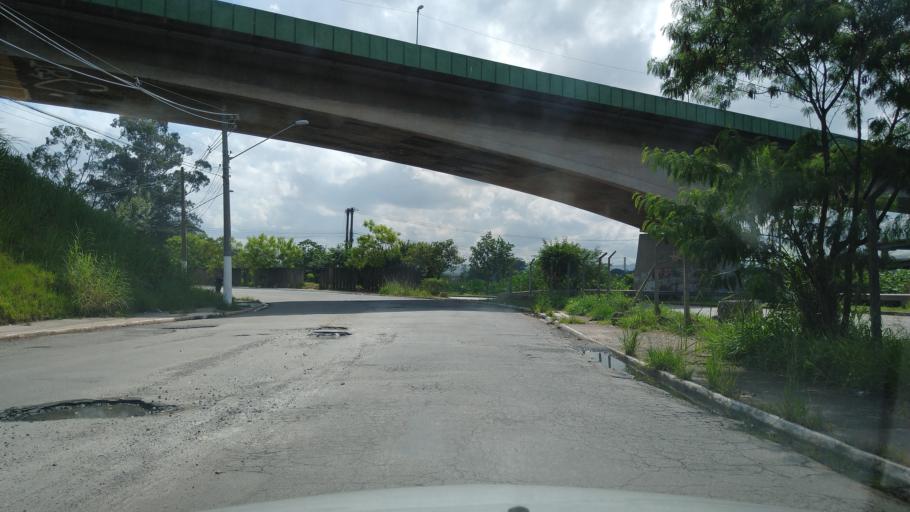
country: BR
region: Sao Paulo
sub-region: Guarulhos
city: Guarulhos
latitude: -23.4818
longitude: -46.4693
